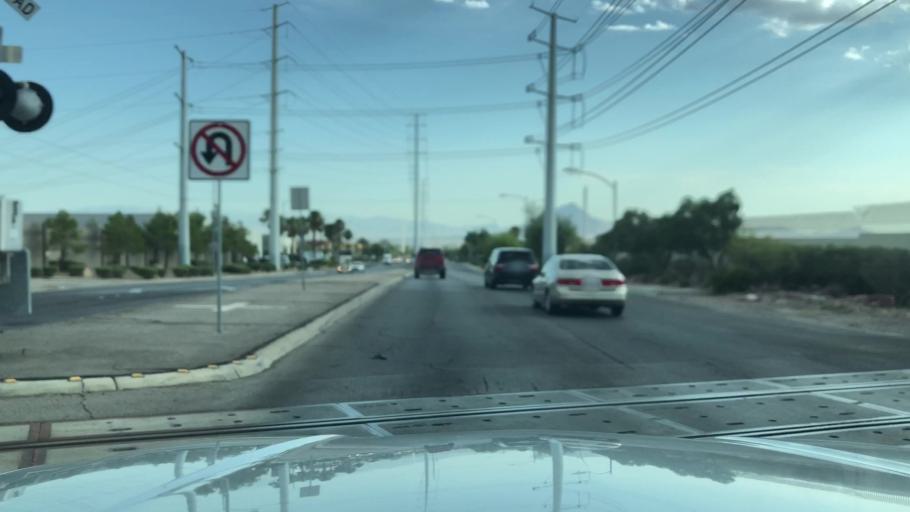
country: US
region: Nevada
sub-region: Clark County
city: Henderson
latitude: 36.0351
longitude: -115.0294
